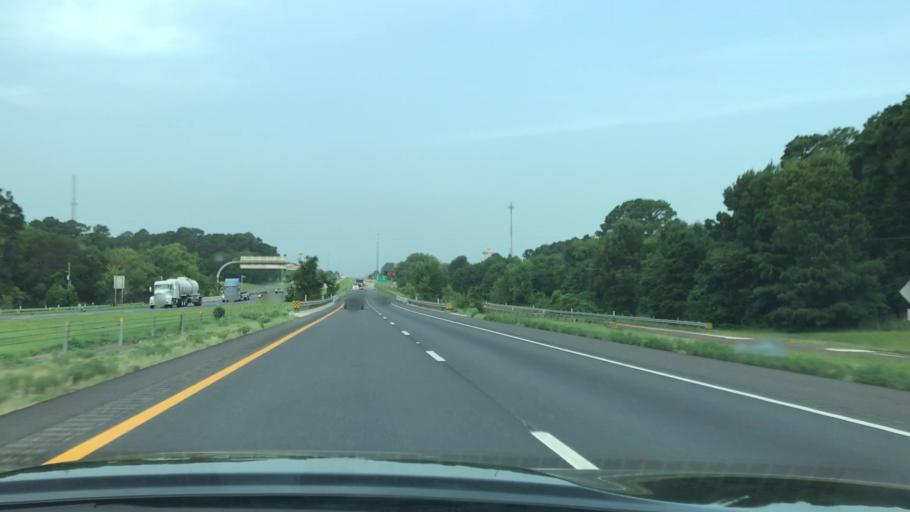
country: US
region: Texas
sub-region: Gregg County
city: Longview
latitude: 32.4543
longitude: -94.6975
